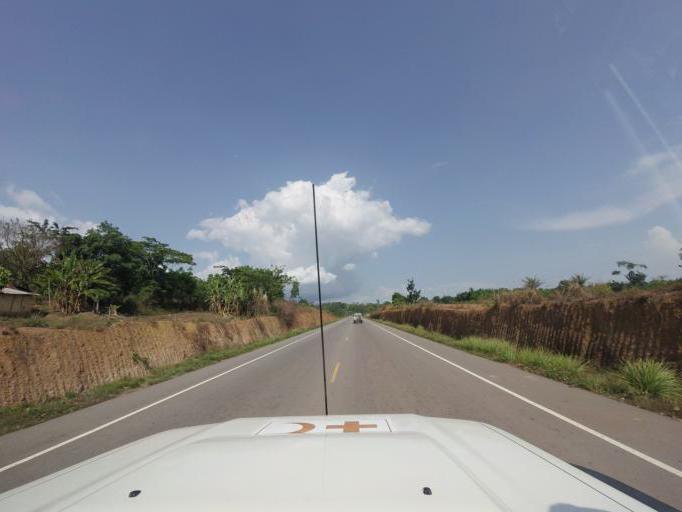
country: LR
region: Bong
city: Gbarnga
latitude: 6.8138
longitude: -9.9221
